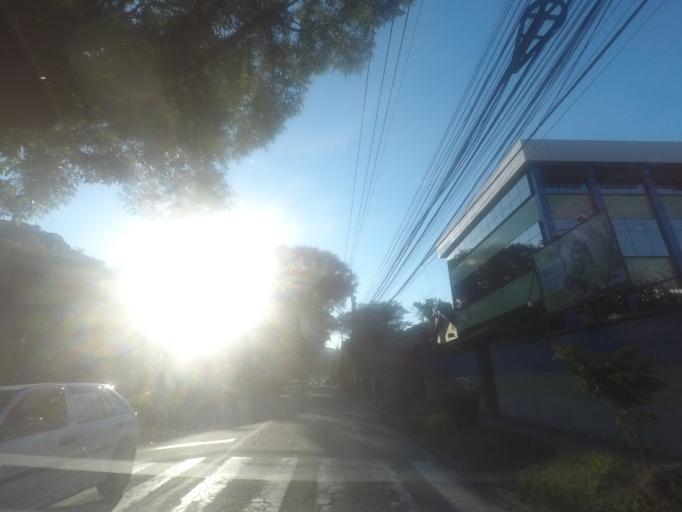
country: BR
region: Rio de Janeiro
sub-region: Petropolis
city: Petropolis
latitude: -22.5278
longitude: -43.1732
